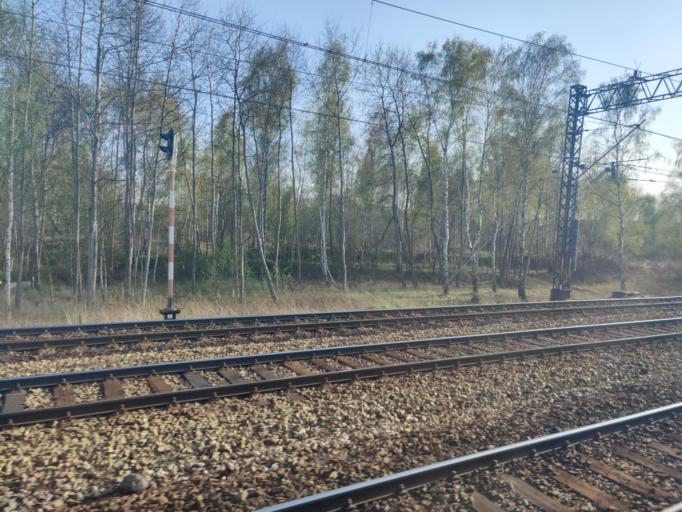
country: PL
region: Silesian Voivodeship
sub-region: Katowice
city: Katowice
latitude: 50.2564
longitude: 19.0696
